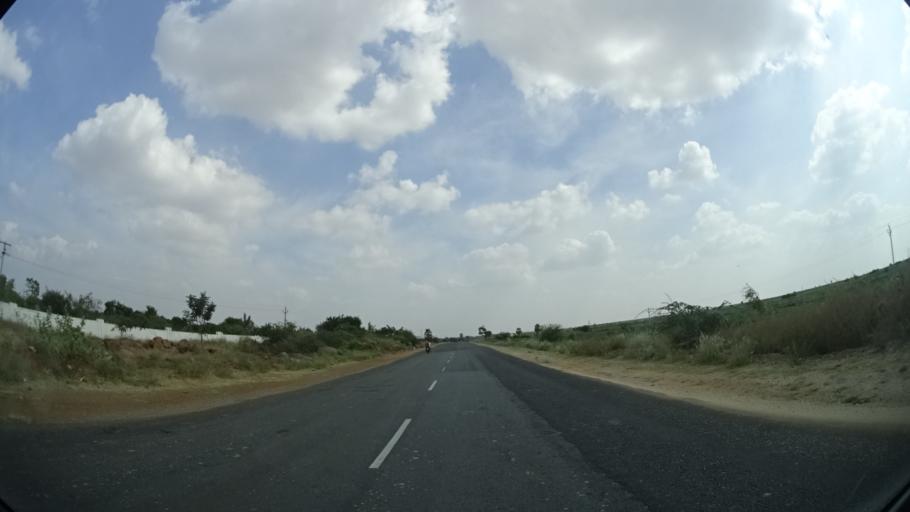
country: IN
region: Andhra Pradesh
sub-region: Anantapur
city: Uravakonda
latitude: 14.7835
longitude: 77.3706
